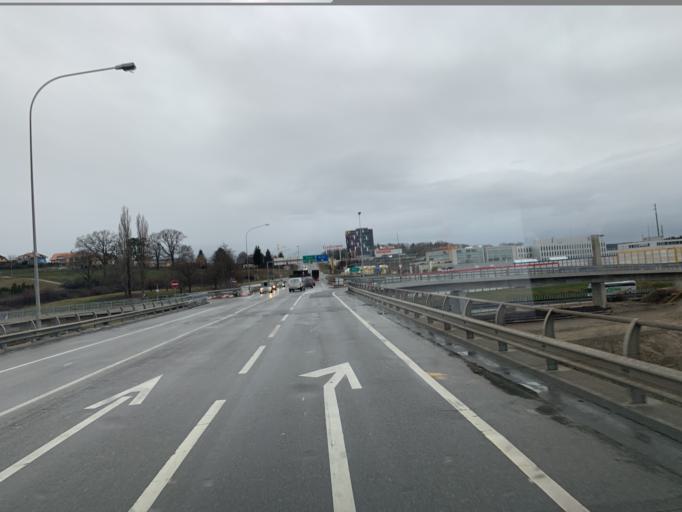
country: CH
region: Fribourg
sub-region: Sarine District
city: Fribourg
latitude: 46.8244
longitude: 7.1490
